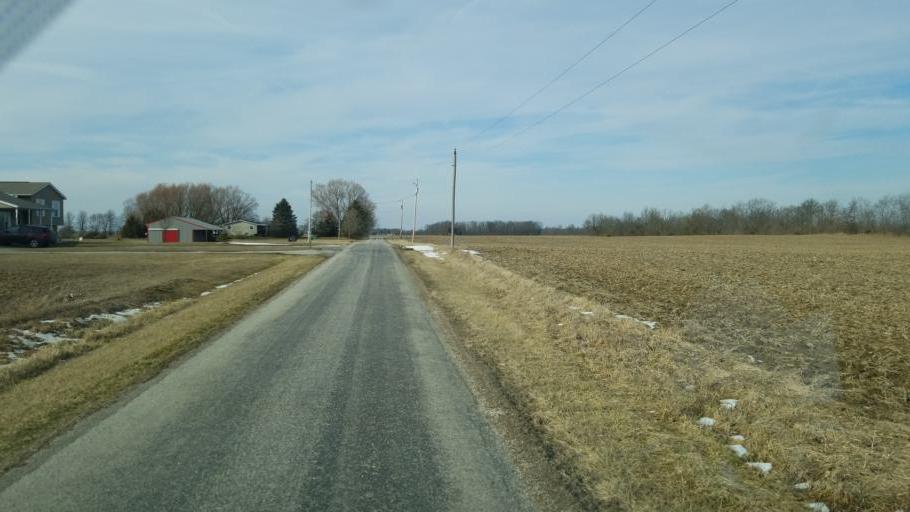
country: US
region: Ohio
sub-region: Marion County
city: Prospect
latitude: 40.3739
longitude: -83.2132
